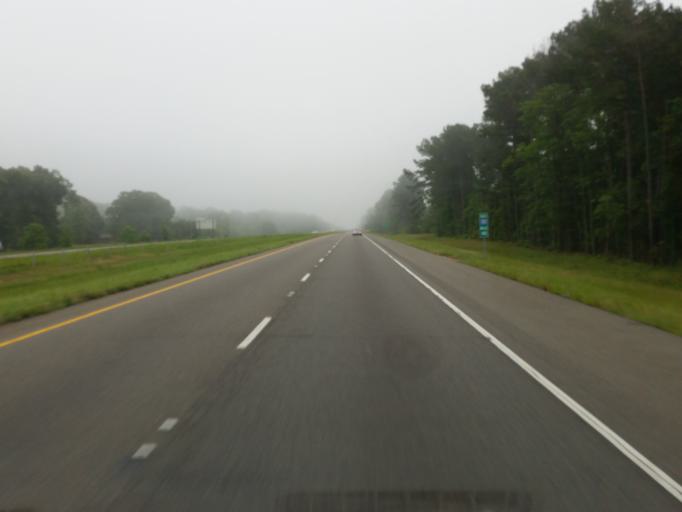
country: US
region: Louisiana
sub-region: Bossier Parish
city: Haughton
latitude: 32.5800
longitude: -93.4190
